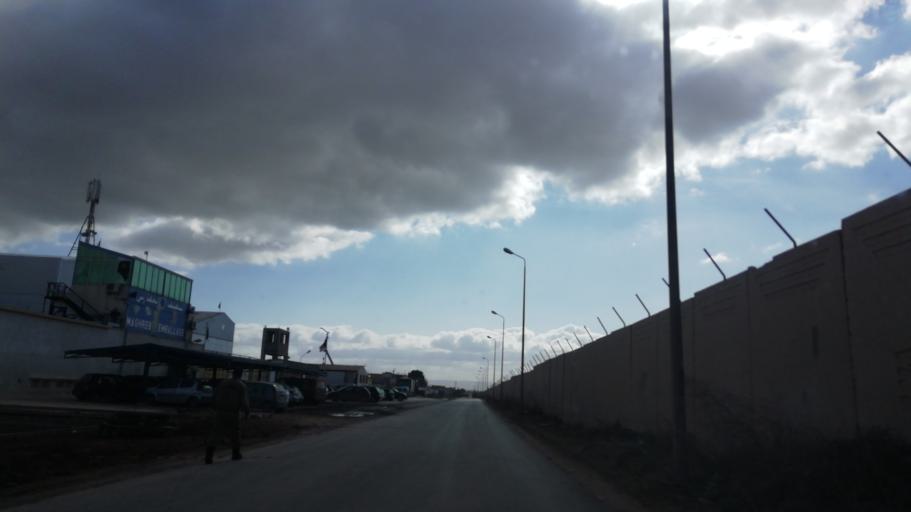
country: DZ
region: Oran
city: Es Senia
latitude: 35.6372
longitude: -0.5982
